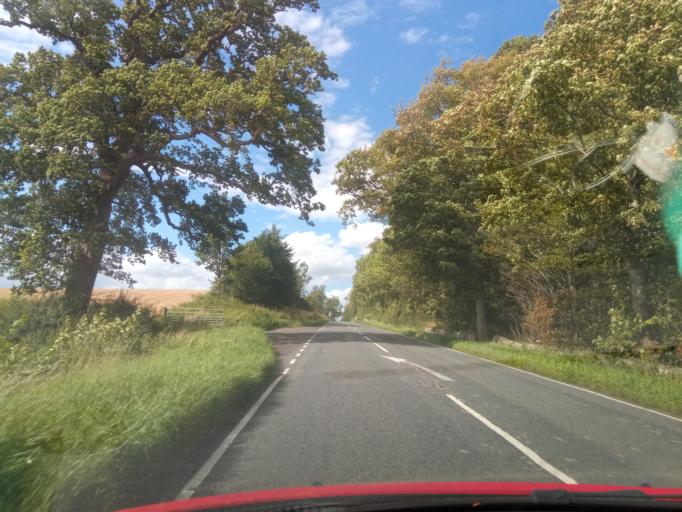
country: GB
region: Scotland
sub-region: The Scottish Borders
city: Coldstream
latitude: 55.6532
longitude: -2.2906
